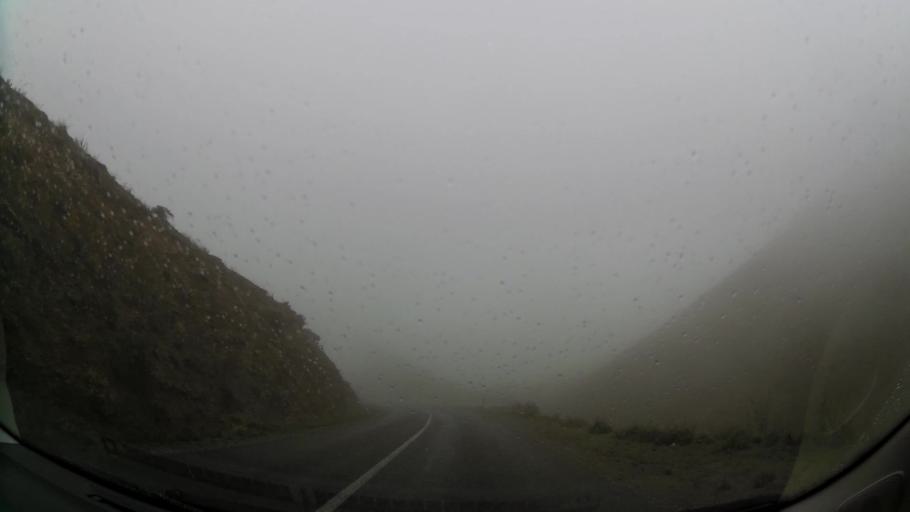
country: MA
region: Oriental
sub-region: Nador
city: Boudinar
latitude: 35.1061
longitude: -3.5640
